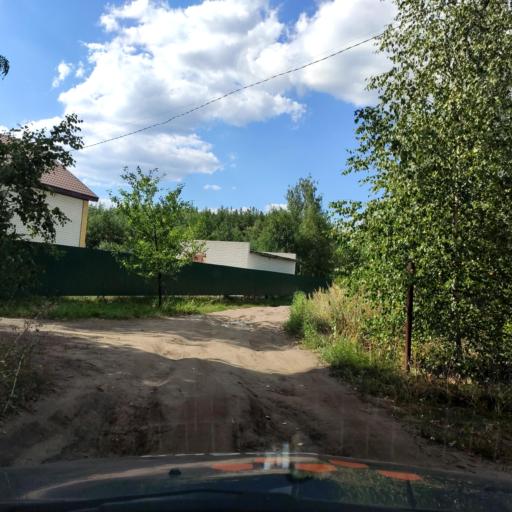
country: RU
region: Voronezj
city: Somovo
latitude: 51.7205
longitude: 39.3987
